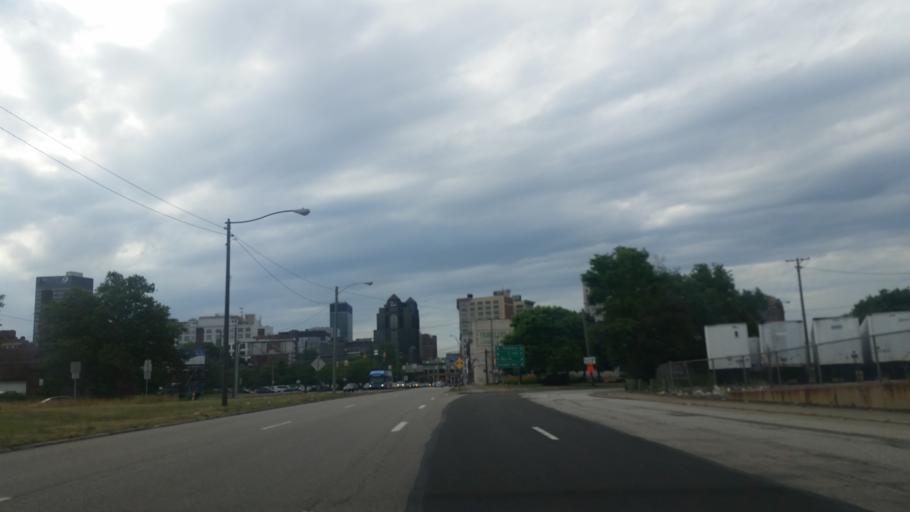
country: US
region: Ohio
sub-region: Cuyahoga County
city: Cleveland
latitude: 41.4965
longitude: -81.6778
